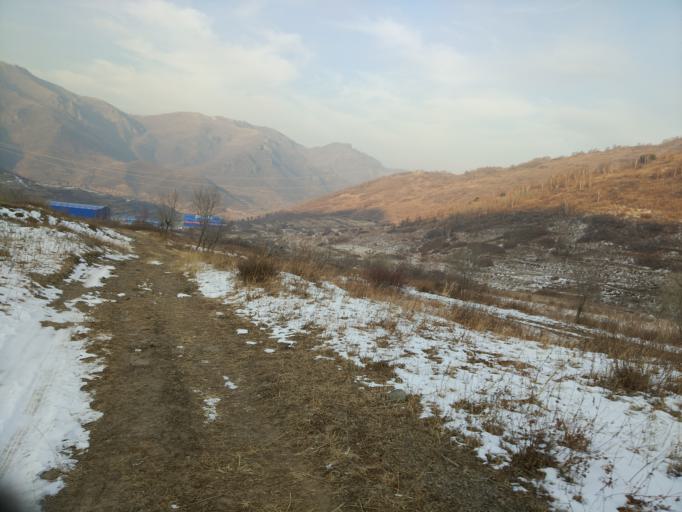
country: CN
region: Hebei
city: Xiwanzi
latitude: 40.8009
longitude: 115.4586
